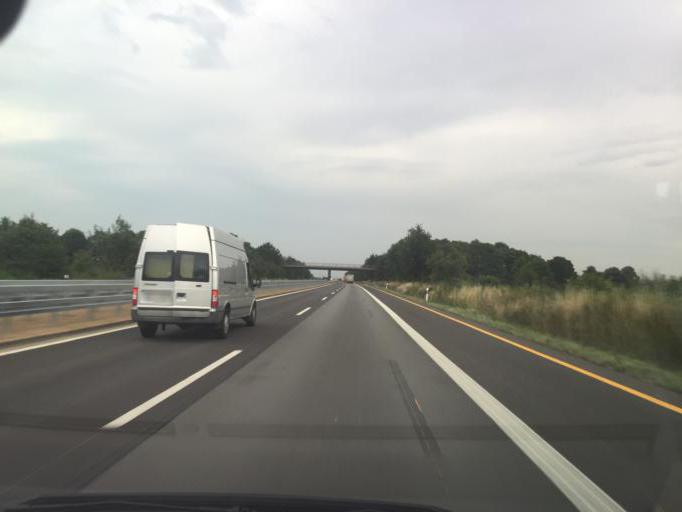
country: DE
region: North Rhine-Westphalia
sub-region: Regierungsbezirk Dusseldorf
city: Nettetal
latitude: 51.2803
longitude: 6.2917
